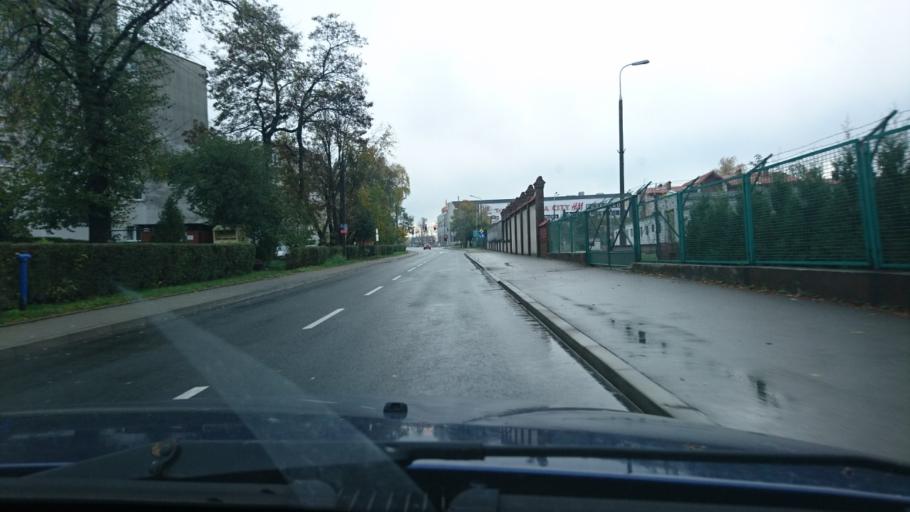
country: PL
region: Silesian Voivodeship
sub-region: Bielsko-Biala
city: Bielsko-Biala
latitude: 49.8056
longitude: 19.0493
